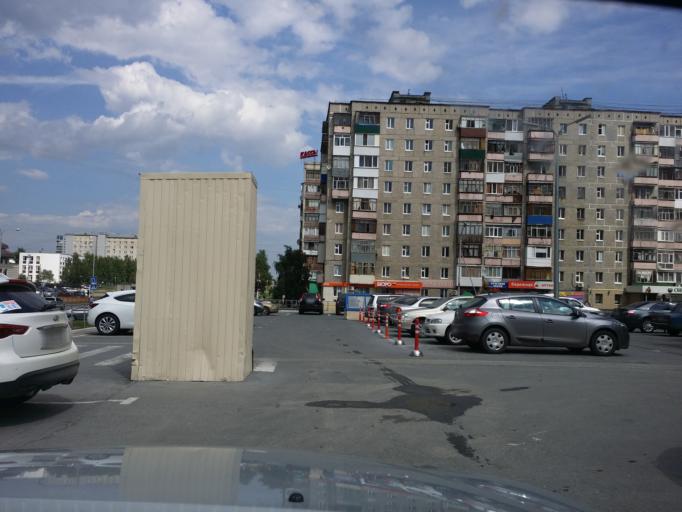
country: RU
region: Khanty-Mansiyskiy Avtonomnyy Okrug
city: Nizhnevartovsk
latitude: 60.9400
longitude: 76.5971
